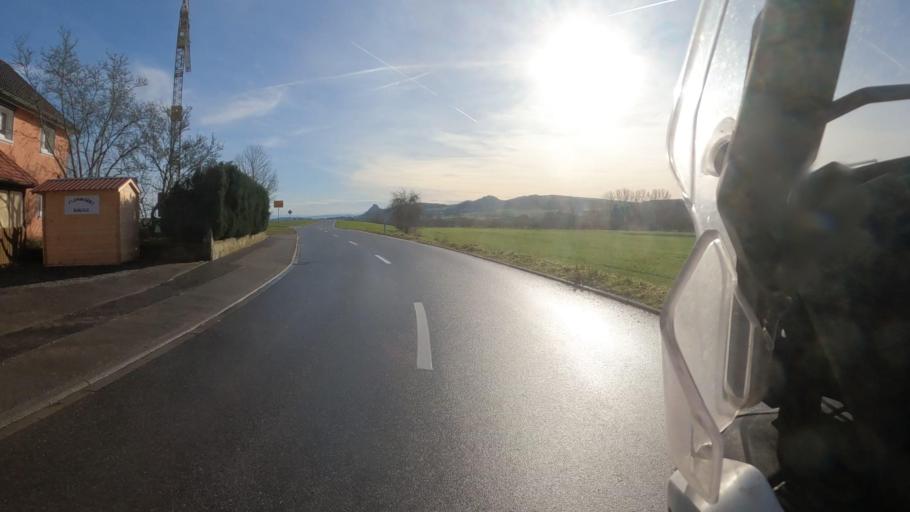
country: DE
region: Baden-Wuerttemberg
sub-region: Freiburg Region
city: Neuhausen
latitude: 47.8349
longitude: 8.7781
